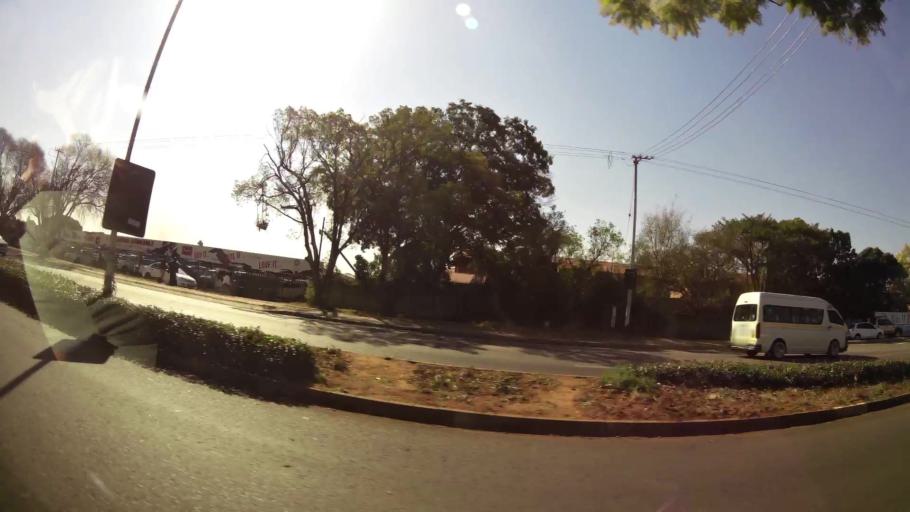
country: ZA
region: Gauteng
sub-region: City of Tshwane Metropolitan Municipality
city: Pretoria
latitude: -25.6774
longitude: 28.1984
